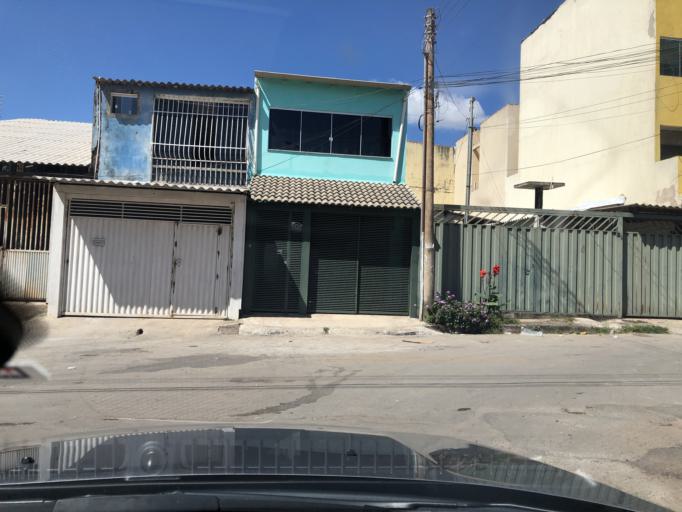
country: BR
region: Federal District
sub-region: Brasilia
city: Brasilia
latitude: -15.8993
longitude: -48.0430
